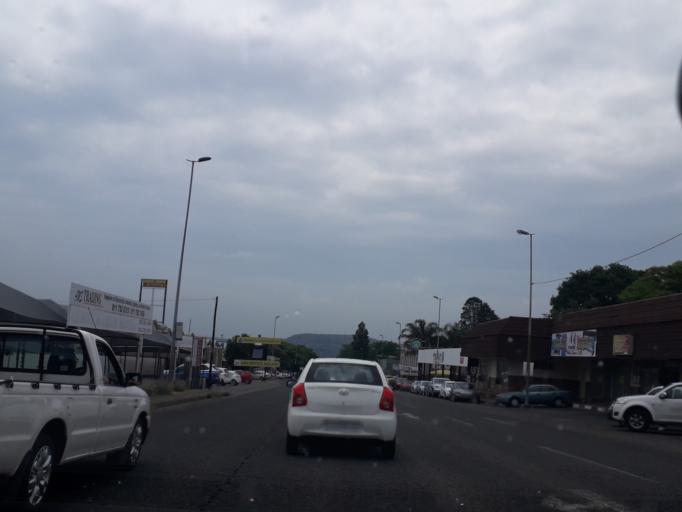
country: ZA
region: Gauteng
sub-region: City of Johannesburg Metropolitan Municipality
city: Johannesburg
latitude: -26.1063
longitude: 27.9812
